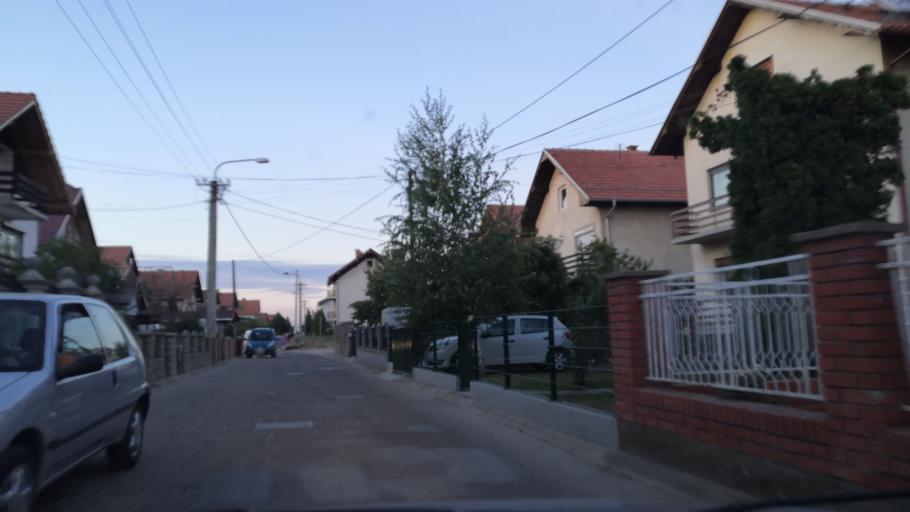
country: RS
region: Central Serbia
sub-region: Borski Okrug
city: Negotin
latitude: 44.2402
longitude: 22.5292
